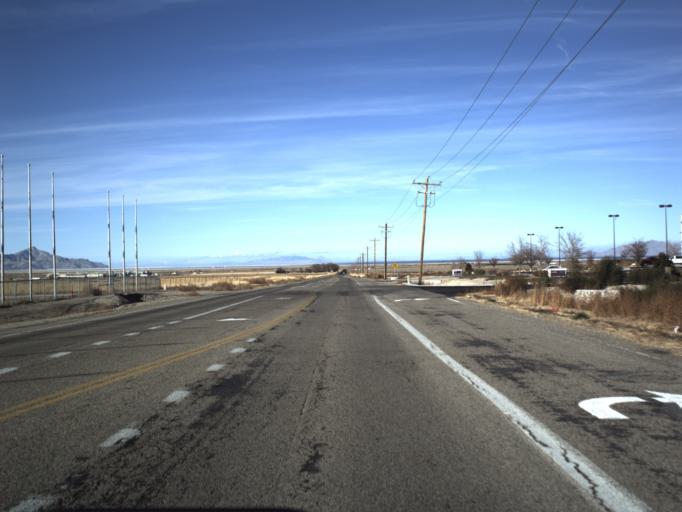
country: US
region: Utah
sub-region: Tooele County
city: Erda
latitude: 40.5856
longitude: -112.3701
